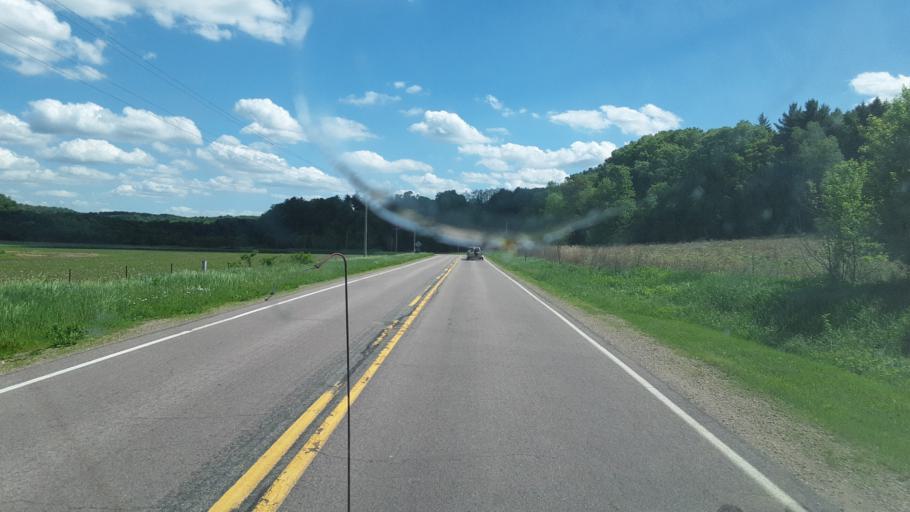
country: US
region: Wisconsin
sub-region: Richland County
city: Richland Center
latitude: 43.4198
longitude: -90.2437
